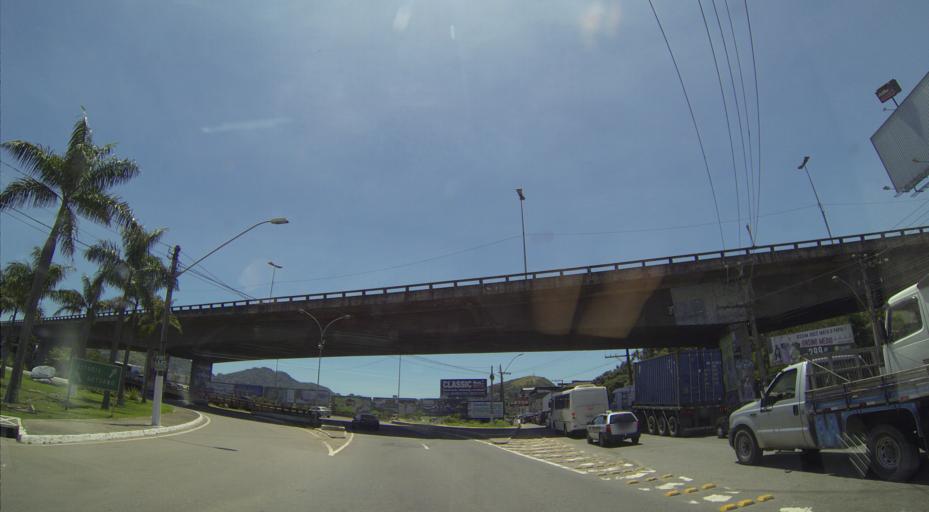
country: BR
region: Espirito Santo
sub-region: Vitoria
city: Vitoria
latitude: -20.3327
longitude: -40.3552
